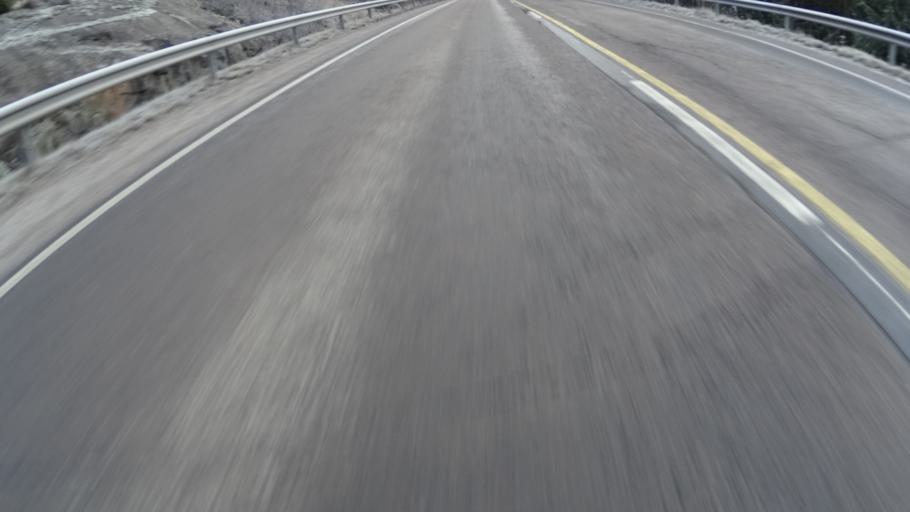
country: FI
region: Uusimaa
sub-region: Helsinki
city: Nurmijaervi
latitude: 60.4313
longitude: 24.7204
